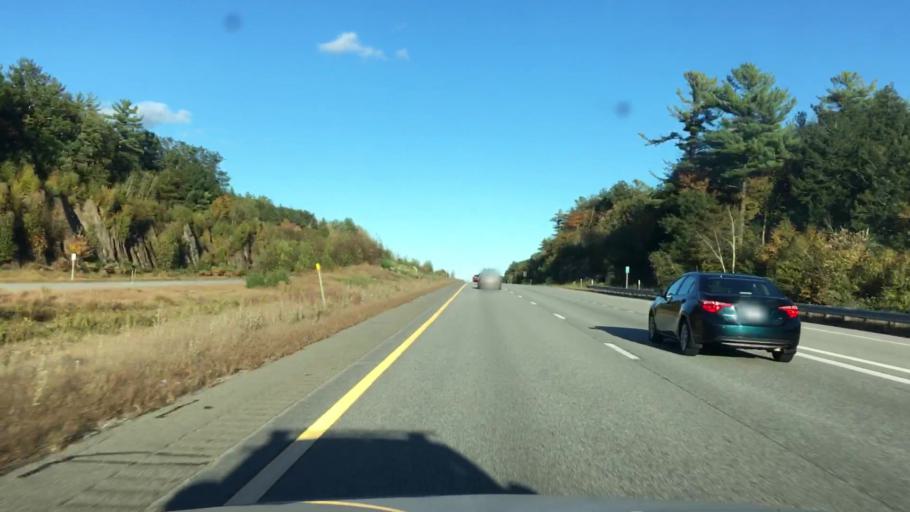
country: US
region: New Hampshire
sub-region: Rockingham County
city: Raymond
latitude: 43.0250
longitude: -71.1899
